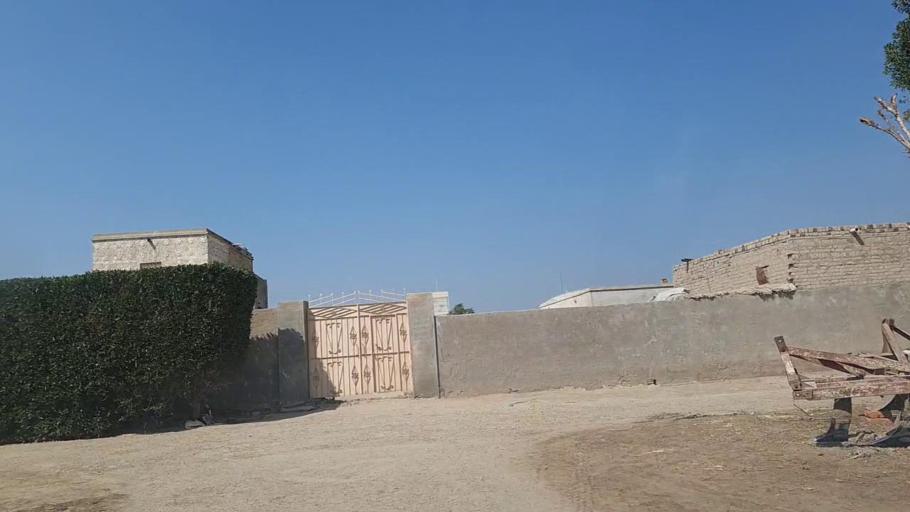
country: PK
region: Sindh
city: Digri
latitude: 25.2125
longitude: 69.1734
